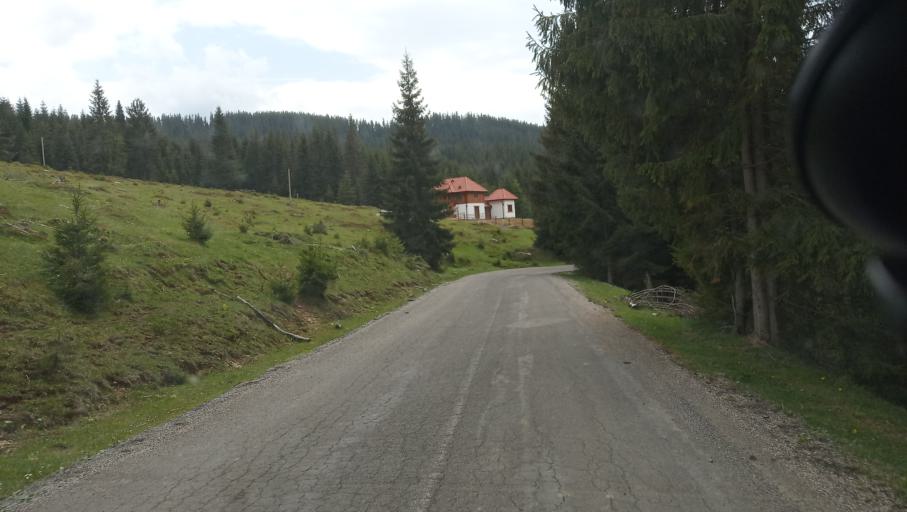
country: RO
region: Alba
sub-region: Comuna Horea
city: Horea
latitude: 46.5484
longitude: 22.8972
